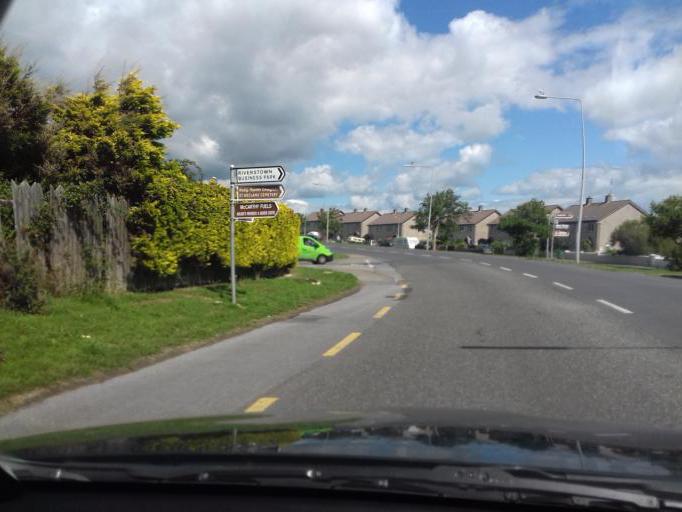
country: IE
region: Munster
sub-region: Waterford
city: Tra Mhor
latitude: 52.1656
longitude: -7.1388
